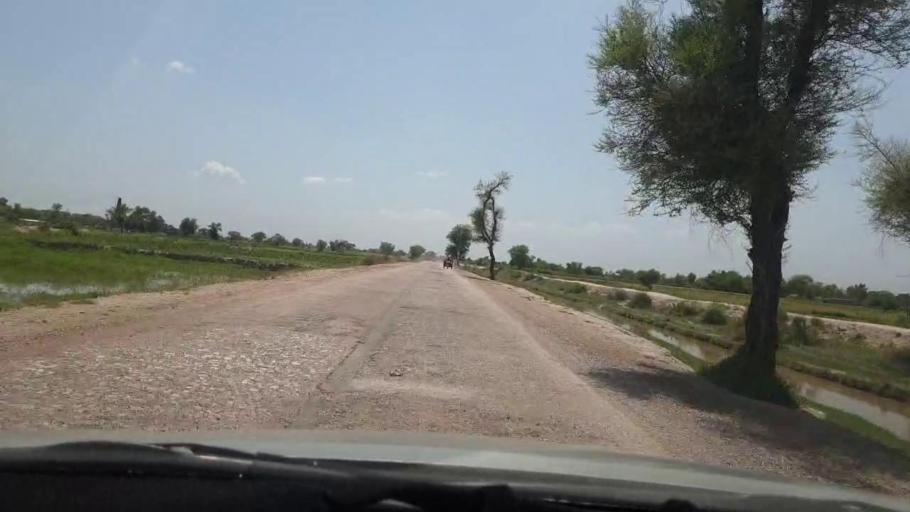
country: PK
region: Sindh
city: Pano Aqil
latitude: 27.7233
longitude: 69.1771
